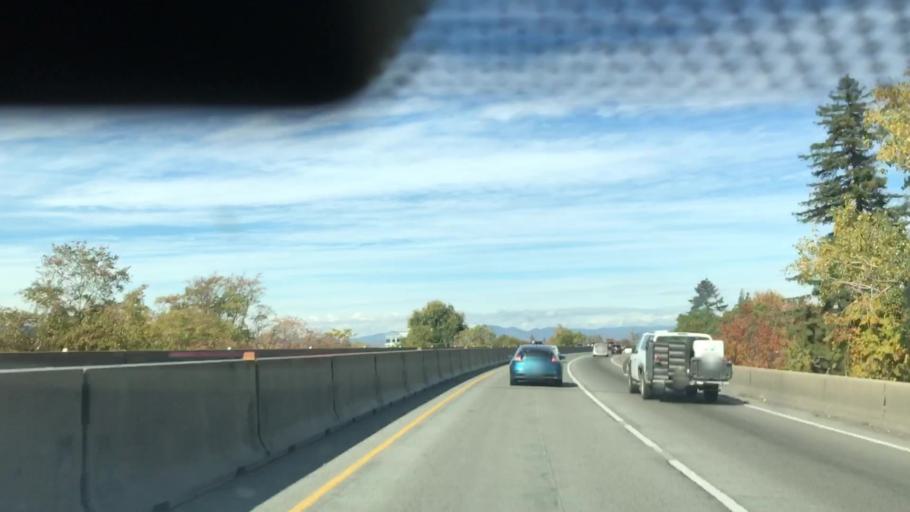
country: US
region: Oregon
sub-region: Jackson County
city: Medford
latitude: 42.3252
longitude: -122.8676
